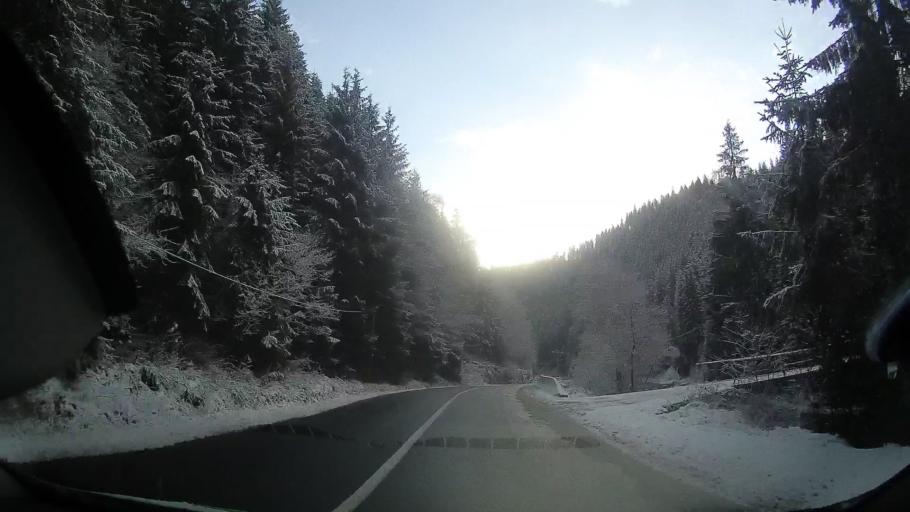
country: RO
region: Alba
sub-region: Comuna Scarisoara
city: Scarisoara
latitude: 46.4554
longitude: 22.8557
